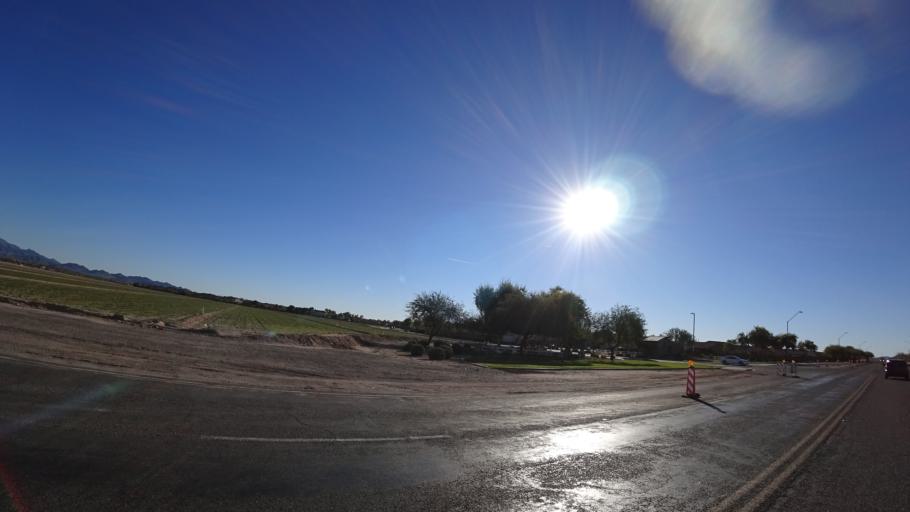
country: US
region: Arizona
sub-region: Maricopa County
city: Goodyear
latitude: 33.4502
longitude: -112.4307
